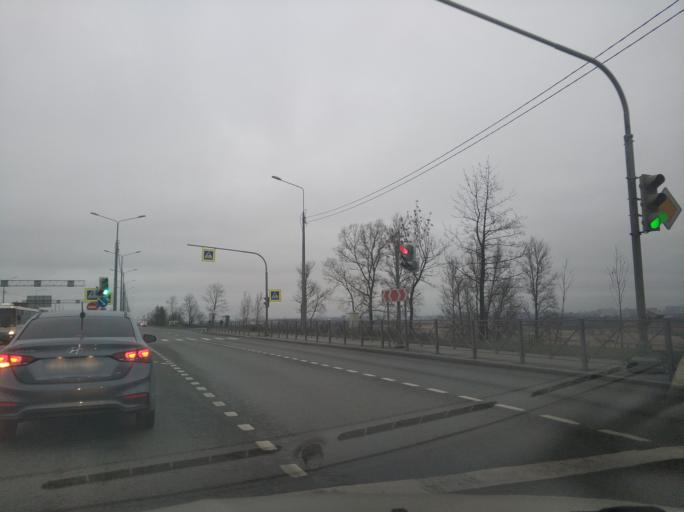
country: RU
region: St.-Petersburg
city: Aleksandrovskaya
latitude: 59.7599
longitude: 30.3708
